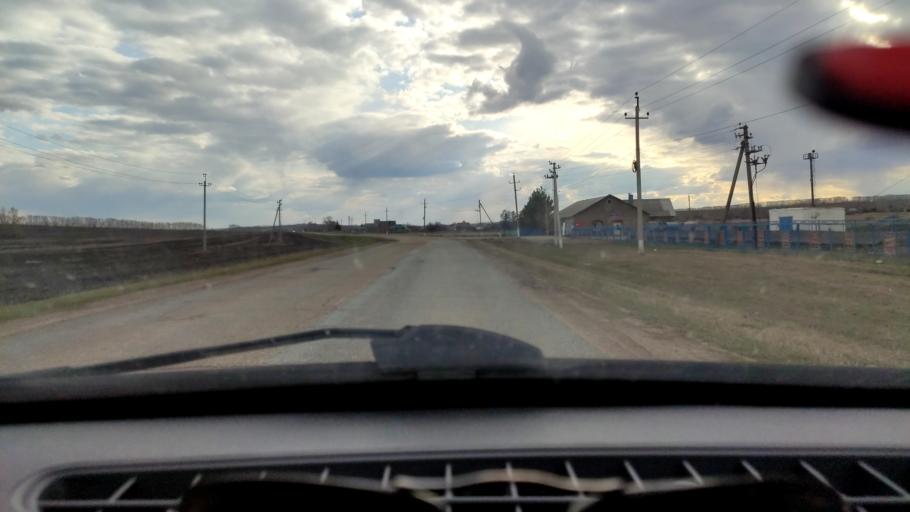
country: RU
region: Bashkortostan
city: Ulukulevo
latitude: 54.4056
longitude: 56.2555
